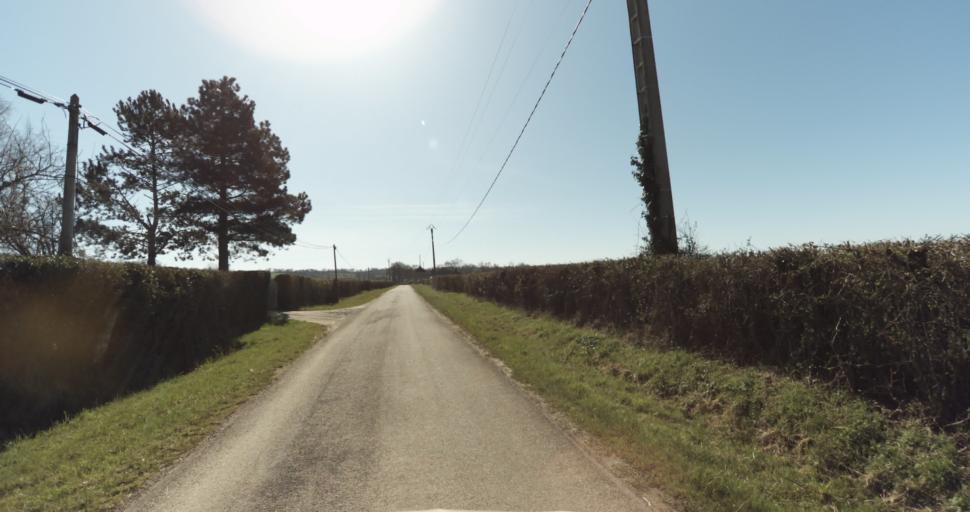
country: FR
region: Lower Normandy
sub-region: Departement de l'Orne
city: Trun
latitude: 48.9331
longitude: 0.0427
